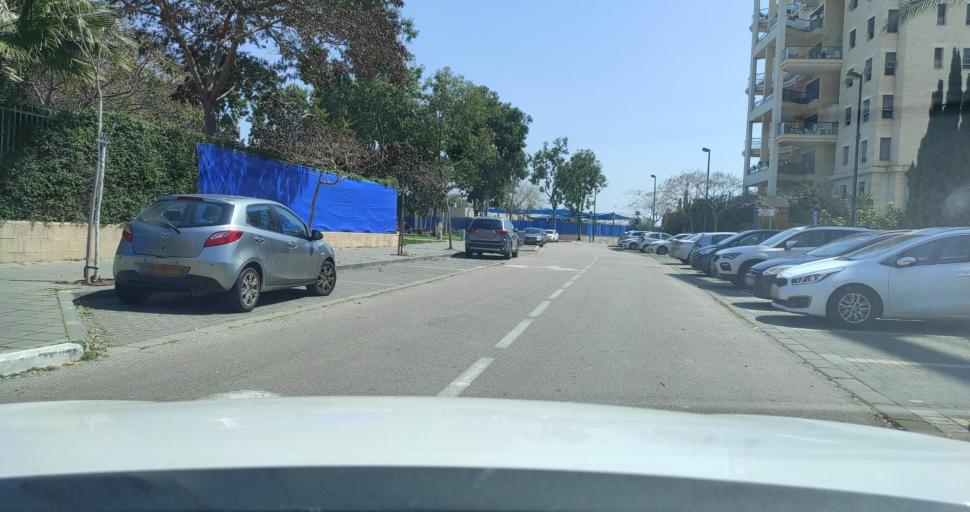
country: IL
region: Central District
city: Nordiyya
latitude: 32.2964
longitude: 34.8707
